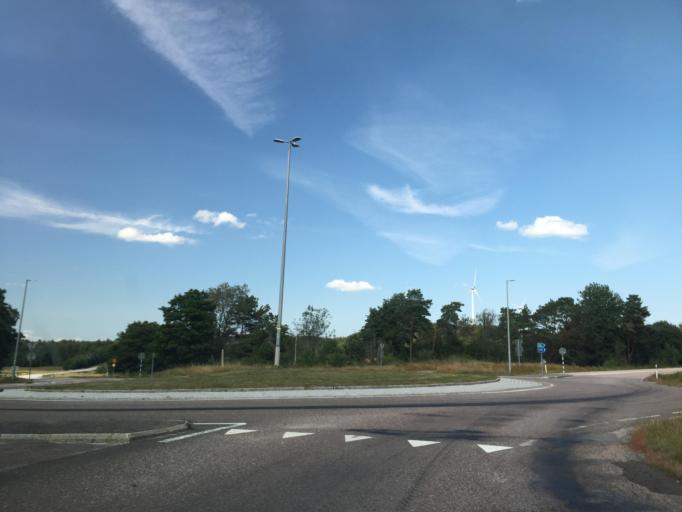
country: SE
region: Vaestra Goetaland
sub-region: Tanums Kommun
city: Tanumshede
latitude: 58.8110
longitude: 11.2641
